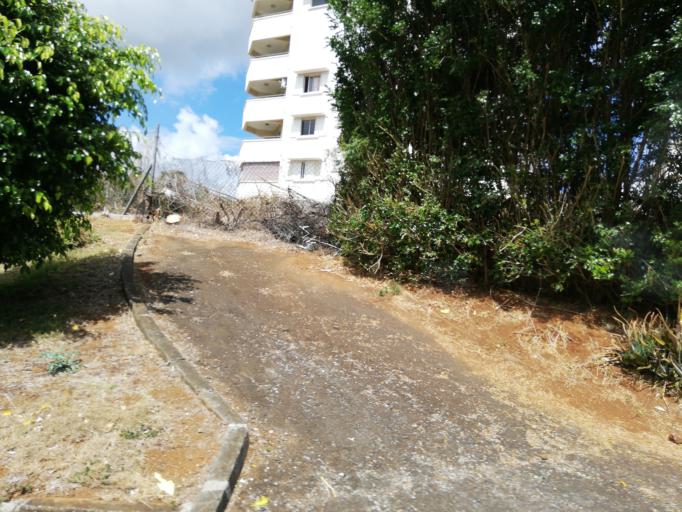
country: MU
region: Moka
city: Moka
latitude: -20.2169
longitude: 57.4760
